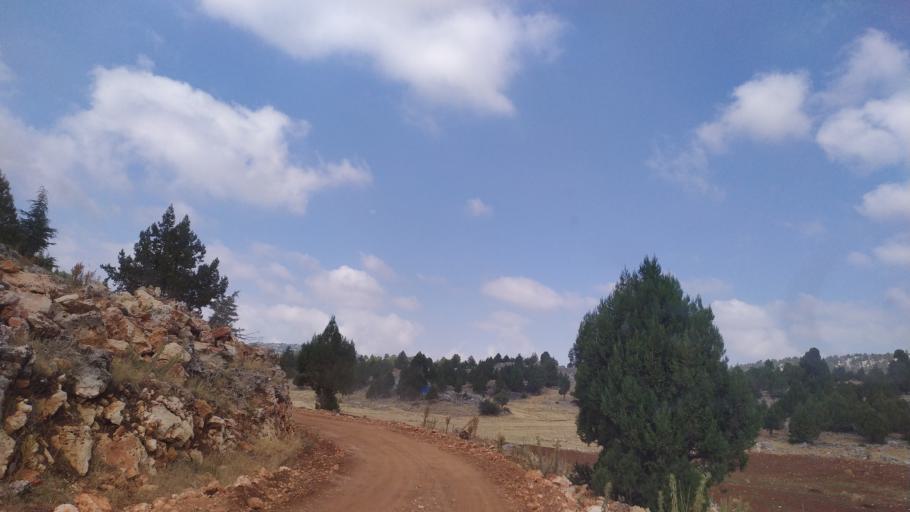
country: TR
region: Mersin
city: Kirobasi
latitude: 36.6211
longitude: 33.8445
